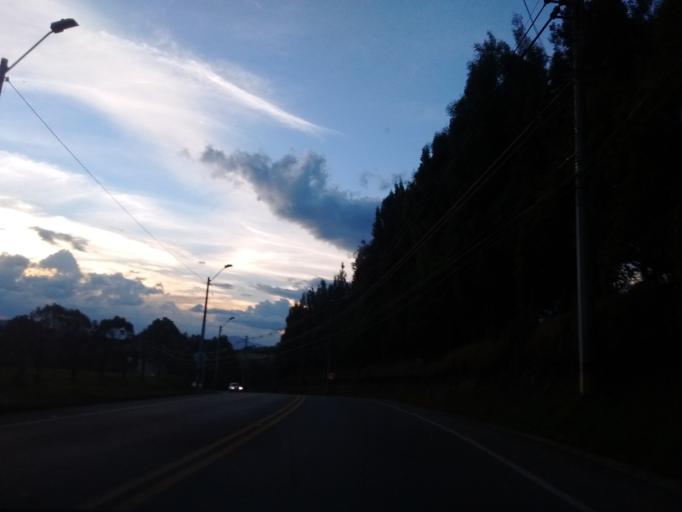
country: CO
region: Antioquia
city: Envigado
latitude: 6.1610
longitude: -75.5087
